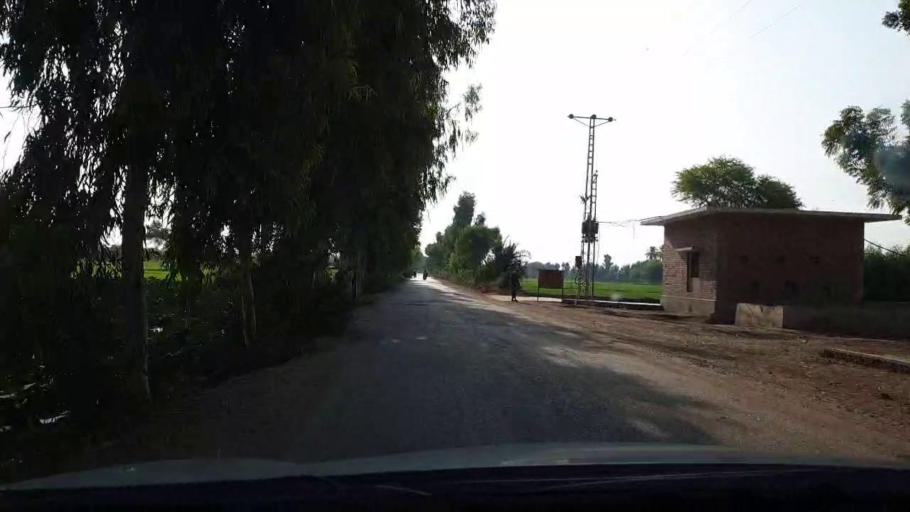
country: PK
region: Sindh
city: Larkana
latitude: 27.5500
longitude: 68.2430
